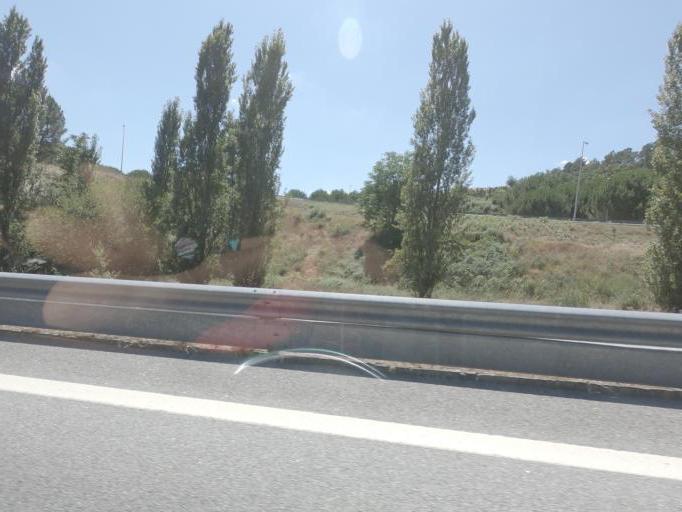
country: PT
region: Porto
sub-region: Amarante
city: Amarante
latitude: 41.2597
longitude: -8.0951
